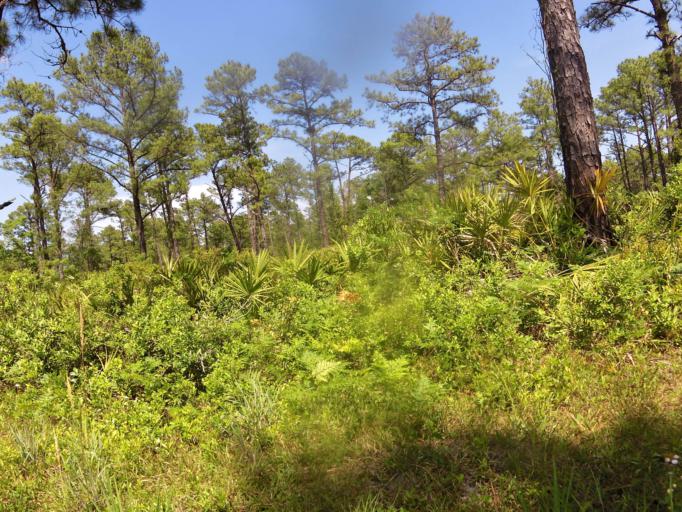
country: US
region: Florida
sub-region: Saint Johns County
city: Palm Valley
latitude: 30.1319
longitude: -81.3777
